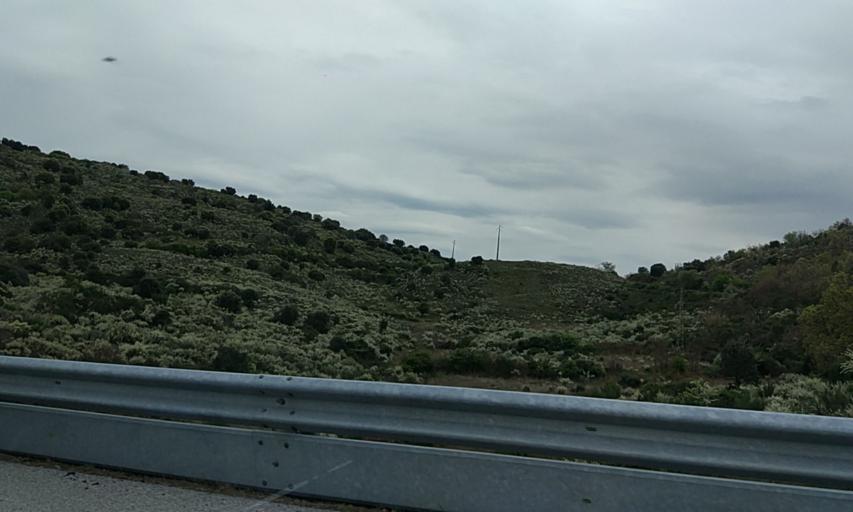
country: PT
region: Guarda
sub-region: Celorico da Beira
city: Celorico da Beira
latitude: 40.6258
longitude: -7.3658
